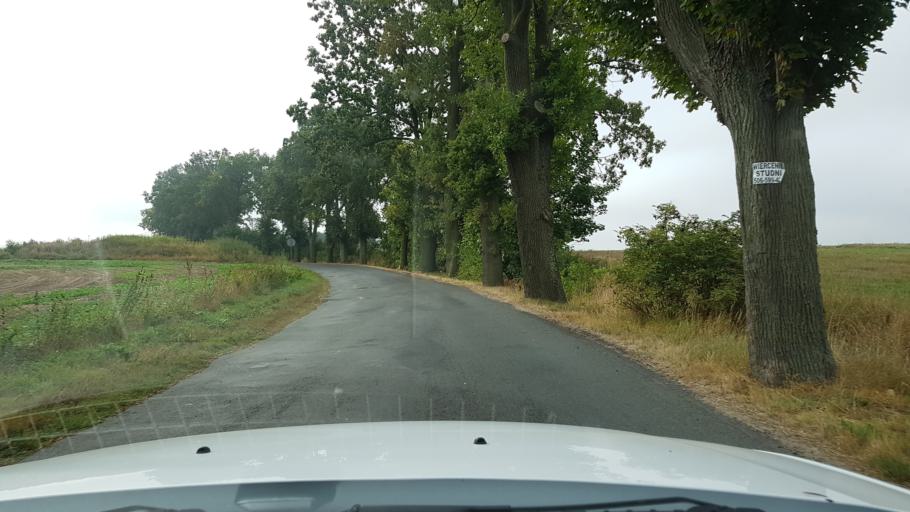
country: PL
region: West Pomeranian Voivodeship
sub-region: Powiat gryfinski
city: Moryn
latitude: 52.8968
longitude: 14.3762
